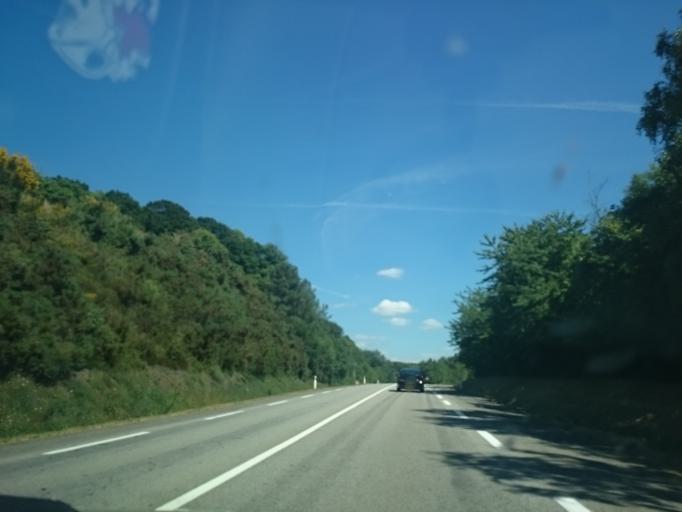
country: FR
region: Brittany
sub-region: Departement des Cotes-d'Armor
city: Mur-de-Bretagne
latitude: 48.2181
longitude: -3.0085
